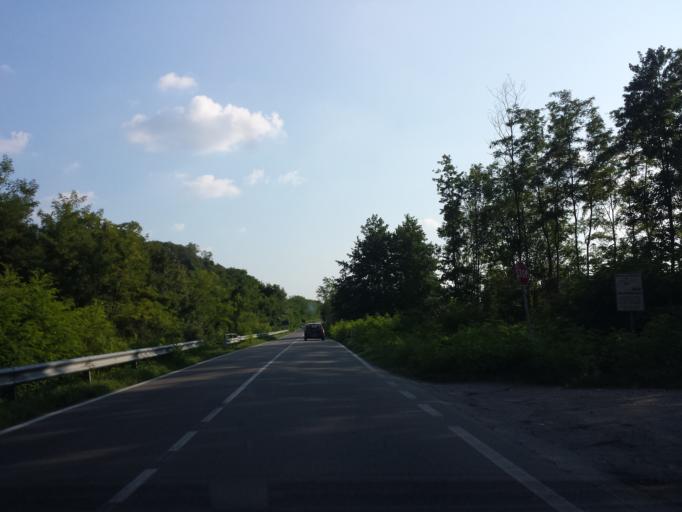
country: IT
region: Lombardy
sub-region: Provincia di Varese
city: Brebbia
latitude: 45.8348
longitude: 8.6290
